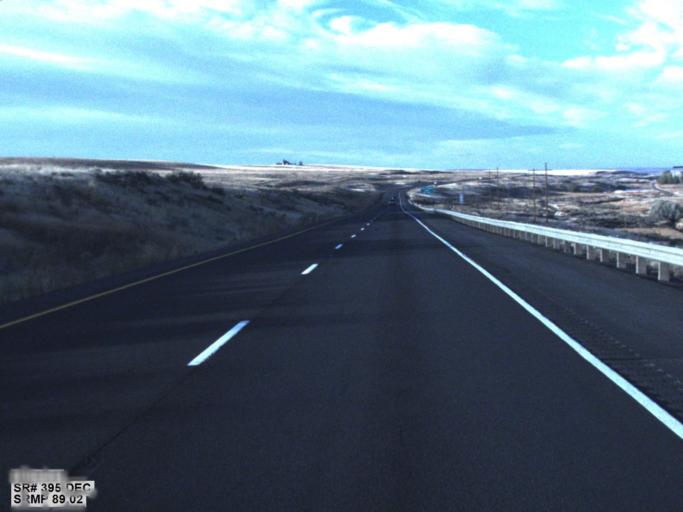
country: US
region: Washington
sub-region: Adams County
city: Ritzville
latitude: 47.0333
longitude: -118.4620
